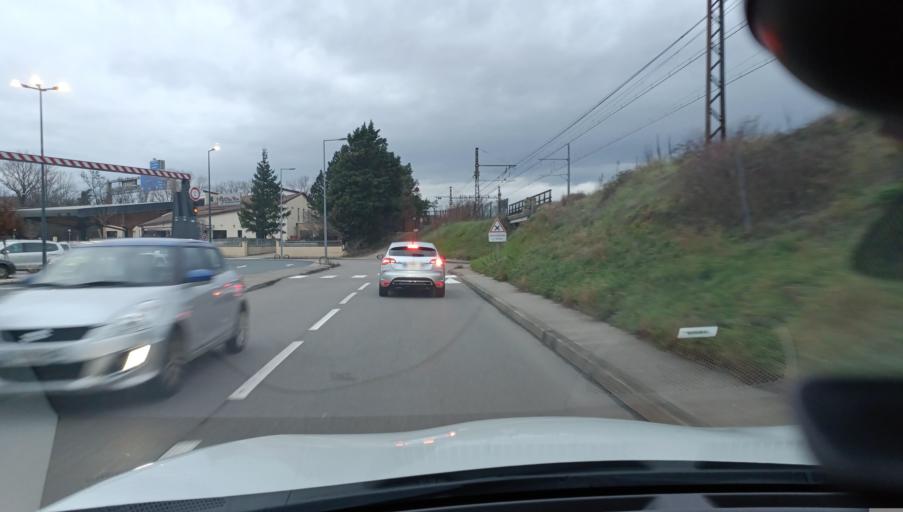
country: FR
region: Rhone-Alpes
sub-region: Departement de l'Isere
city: Chasse-sur-Rhone
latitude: 45.5771
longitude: 4.8069
